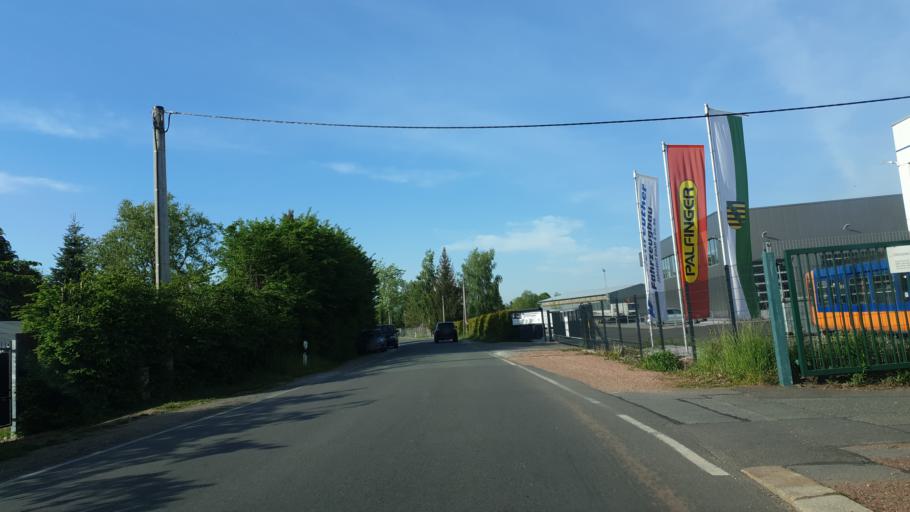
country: DE
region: Saxony
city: Jahnsdorf
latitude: 50.7577
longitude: 12.8599
